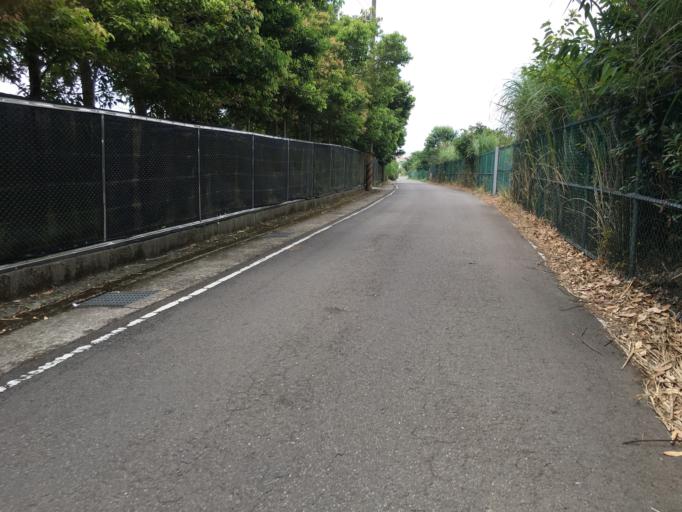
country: TW
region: Taiwan
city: Daxi
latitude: 24.8282
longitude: 121.2139
